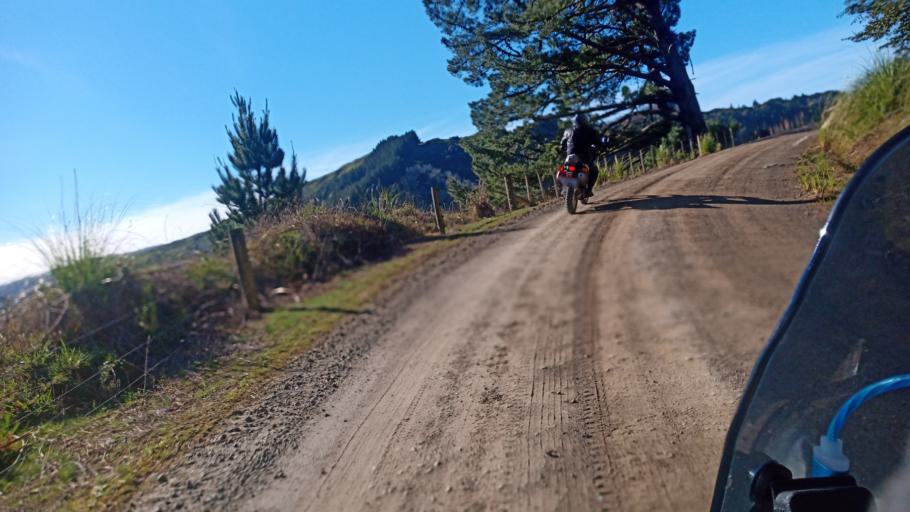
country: NZ
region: Gisborne
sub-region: Gisborne District
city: Gisborne
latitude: -38.2864
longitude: 177.8539
